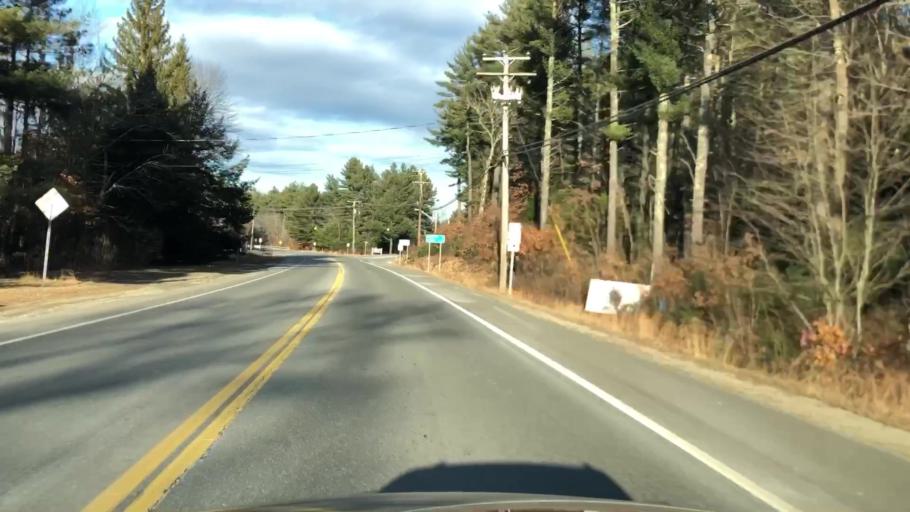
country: US
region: New Hampshire
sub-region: Hillsborough County
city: Brookline
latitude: 42.7127
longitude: -71.6642
